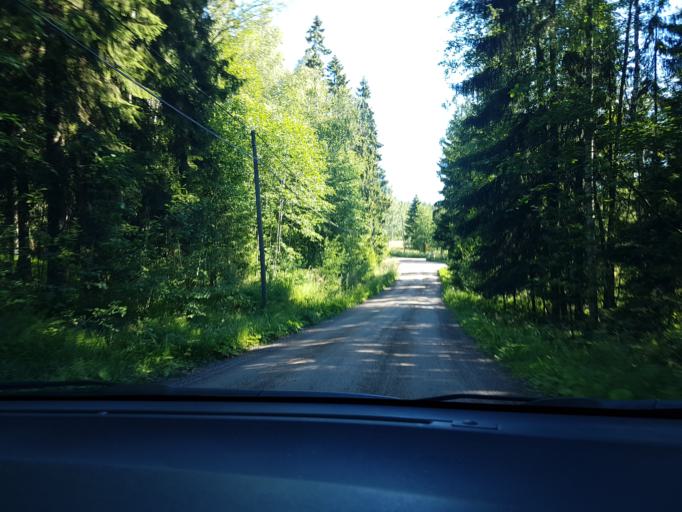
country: FI
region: Uusimaa
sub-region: Helsinki
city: Sibbo
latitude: 60.2876
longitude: 25.2397
